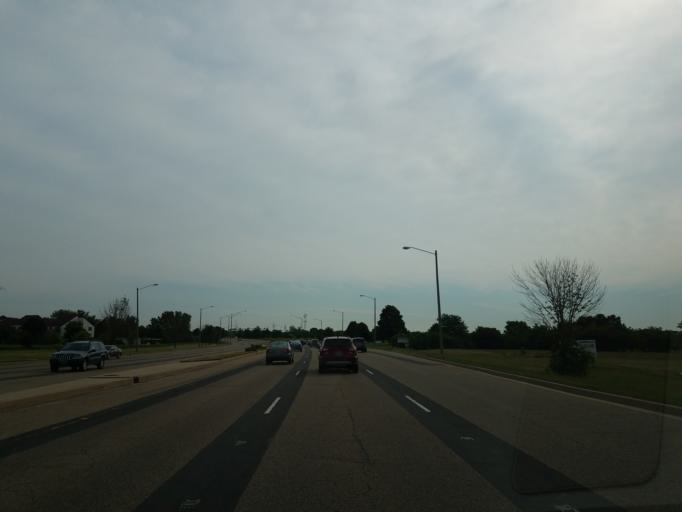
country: US
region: Illinois
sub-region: McLean County
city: Bloomington
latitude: 40.4620
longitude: -88.9604
